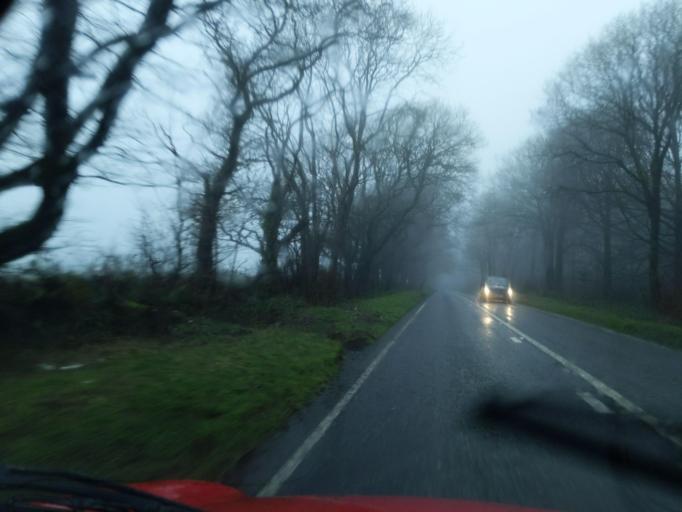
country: GB
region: England
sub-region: Cornwall
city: Callington
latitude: 50.5246
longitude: -4.3216
